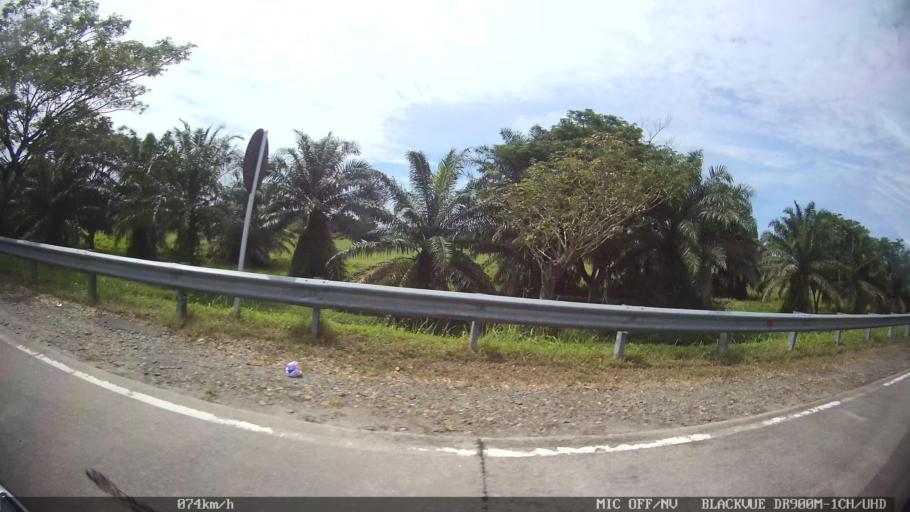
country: ID
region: North Sumatra
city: Percut
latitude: 3.6298
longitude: 98.8750
